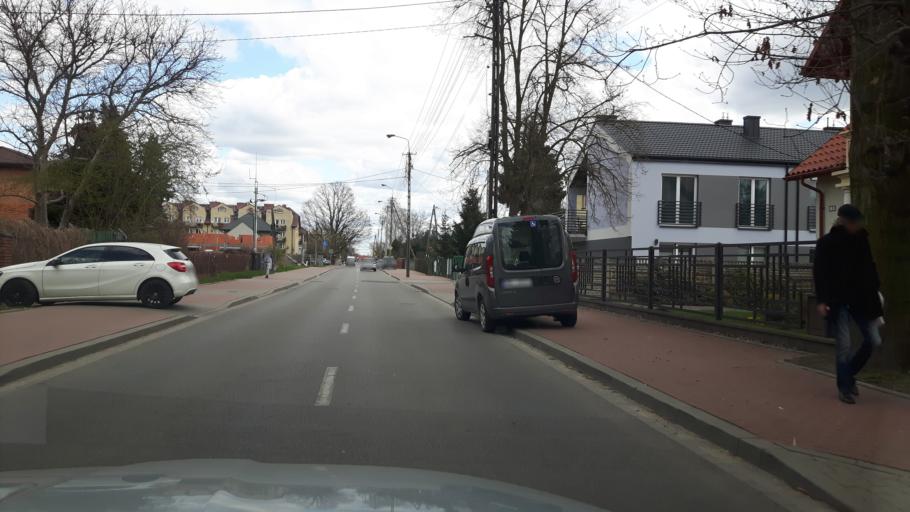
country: PL
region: Masovian Voivodeship
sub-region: Powiat wolominski
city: Wolomin
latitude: 52.3436
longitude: 21.2551
